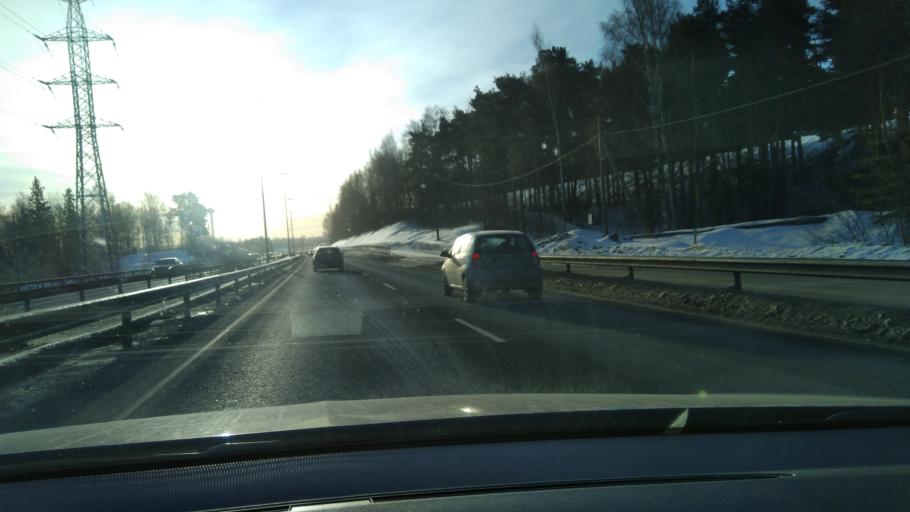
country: FI
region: Pirkanmaa
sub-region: Tampere
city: Pirkkala
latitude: 61.5083
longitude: 23.6987
